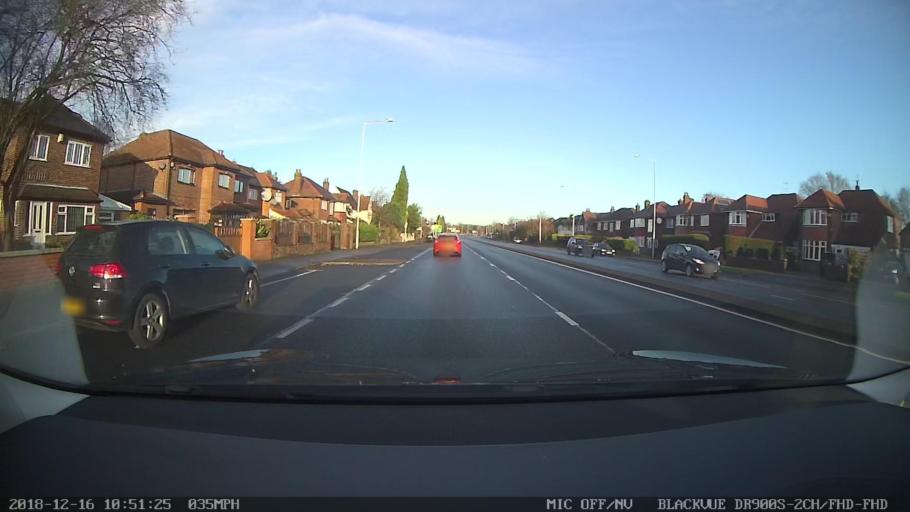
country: GB
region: England
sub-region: Manchester
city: Didsbury
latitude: 53.3880
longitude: -2.2249
